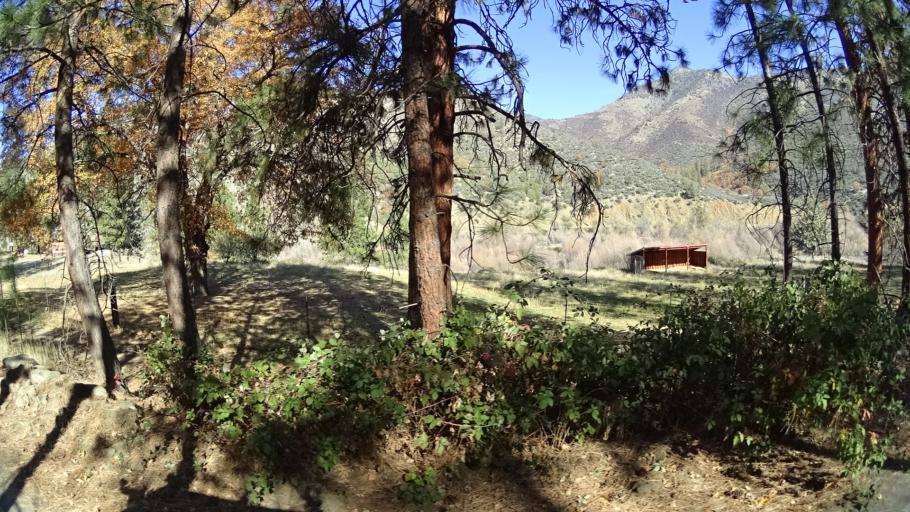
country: US
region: California
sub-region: Siskiyou County
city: Yreka
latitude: 41.8408
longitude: -122.6752
